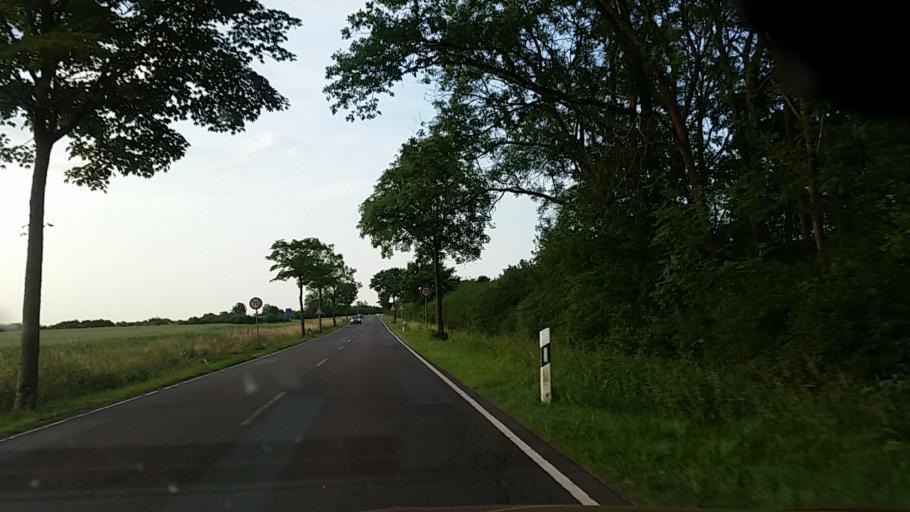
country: DE
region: Lower Saxony
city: Rennau
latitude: 52.2865
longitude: 10.9155
